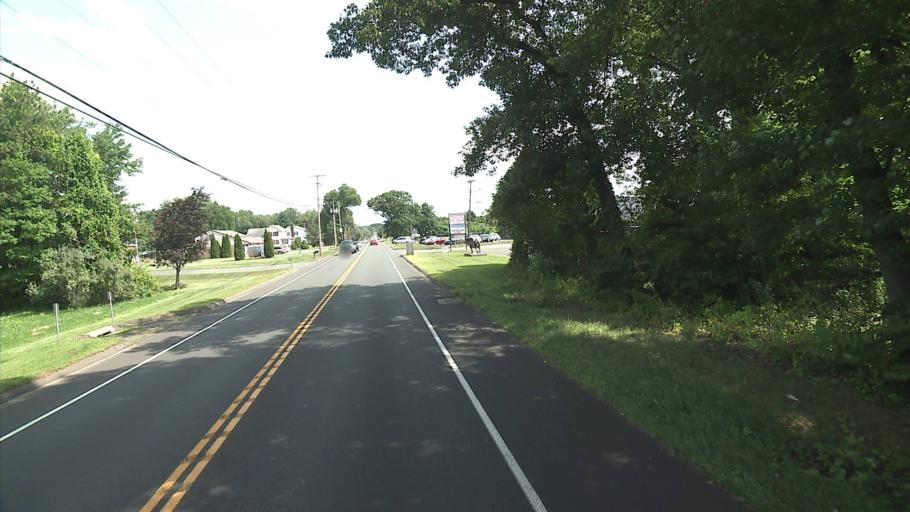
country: US
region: Connecticut
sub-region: Hartford County
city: South Windsor
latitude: 41.8504
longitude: -72.5769
